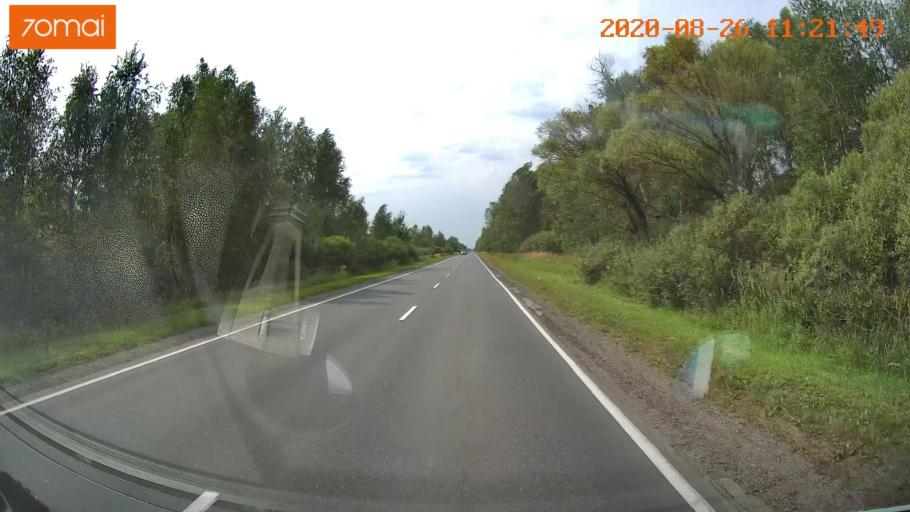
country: RU
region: Rjazan
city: Shilovo
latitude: 54.3717
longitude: 41.0382
